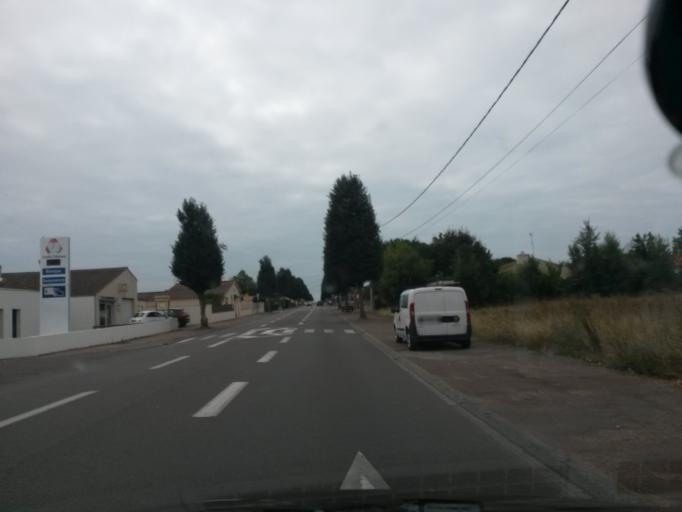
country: FR
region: Pays de la Loire
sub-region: Departement de la Vendee
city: Olonne-sur-Mer
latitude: 46.5310
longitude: -1.7742
